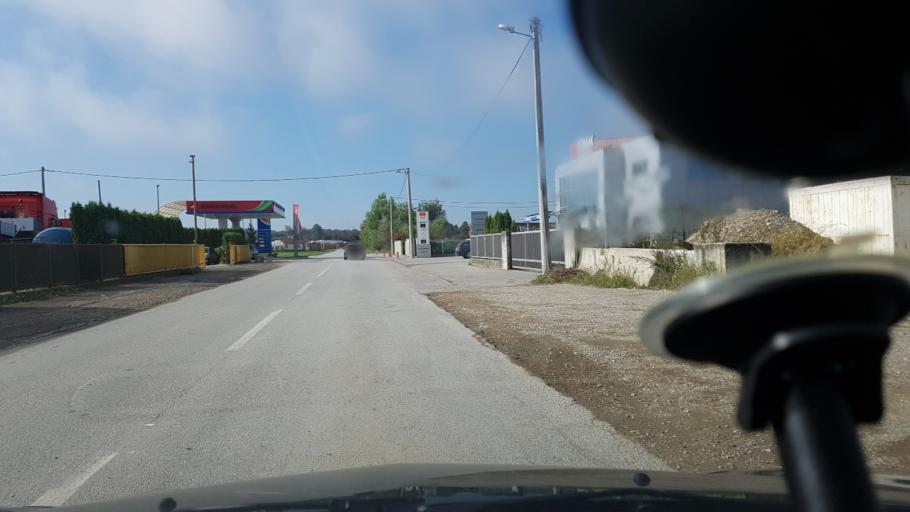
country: HR
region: Zagrebacka
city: Rakitje
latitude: 45.7795
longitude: 15.8286
